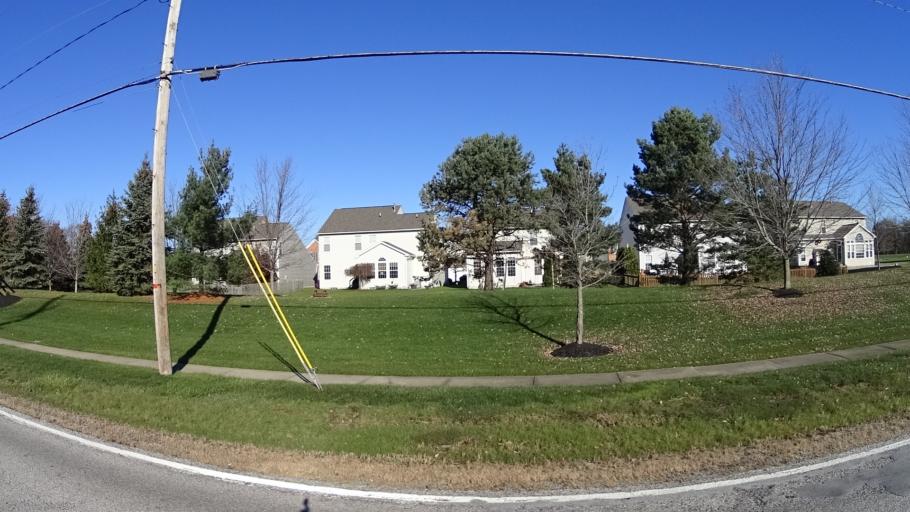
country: US
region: Ohio
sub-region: Cuyahoga County
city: Bay Village
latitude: 41.4781
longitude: -81.9716
